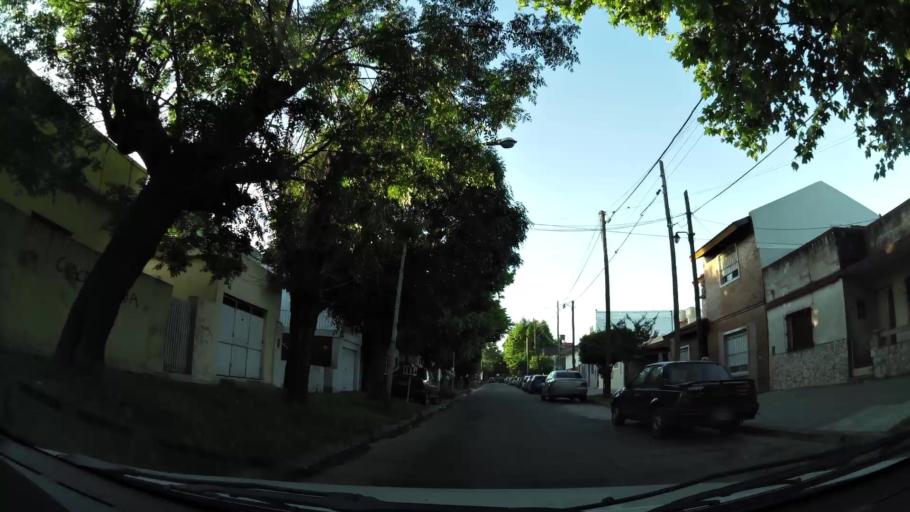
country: AR
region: Buenos Aires
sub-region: Partido de General San Martin
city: General San Martin
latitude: -34.5675
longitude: -58.5225
